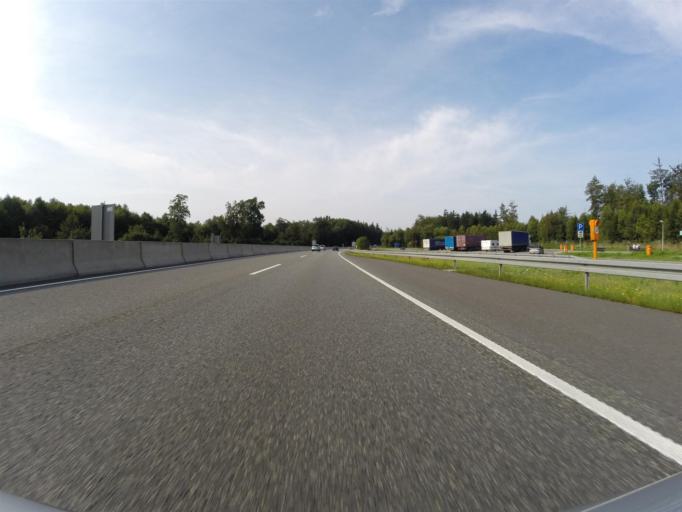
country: DE
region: Hesse
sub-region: Regierungsbezirk Kassel
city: Friedewald
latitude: 50.8979
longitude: 9.8628
